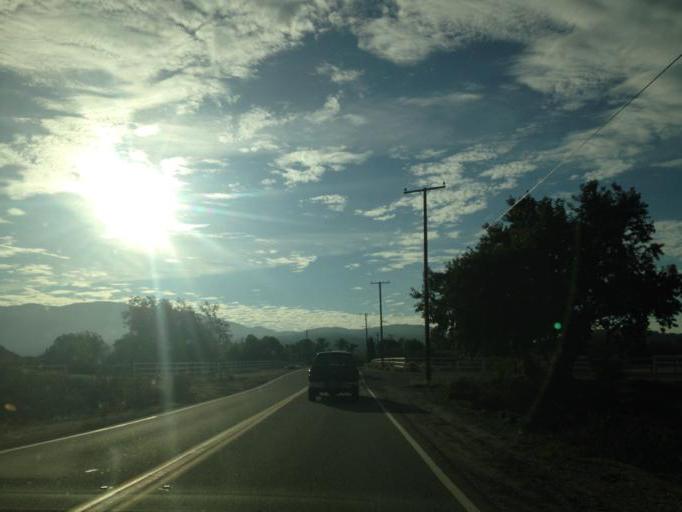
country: US
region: California
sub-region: San Diego County
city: Rainbow
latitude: 33.4484
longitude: -117.0940
